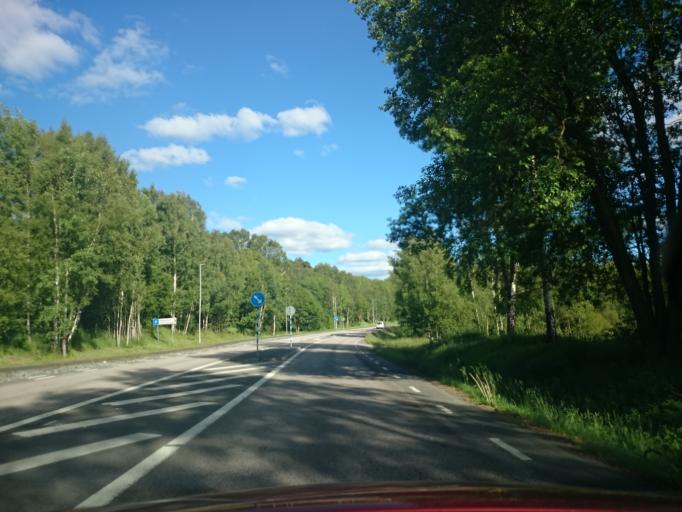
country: SE
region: Vaestra Goetaland
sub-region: Harryda Kommun
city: Molnlycke
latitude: 57.6726
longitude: 12.0847
